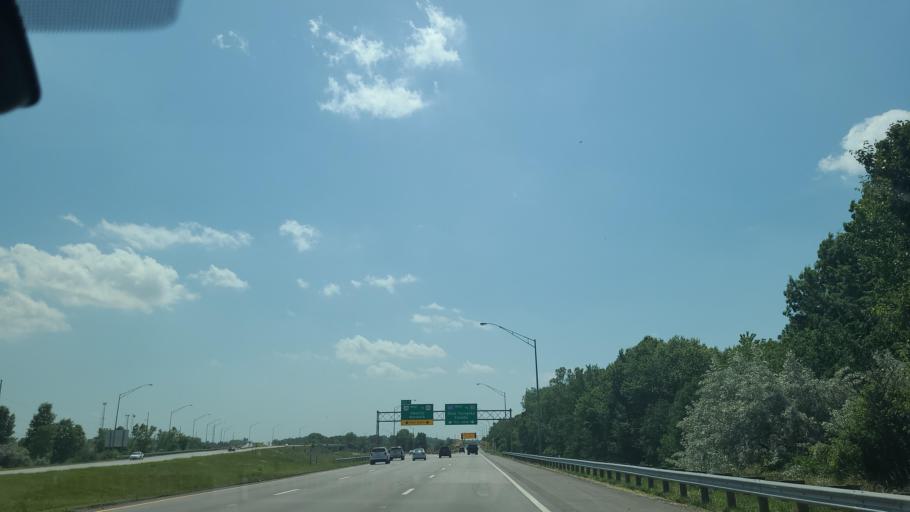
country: US
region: Ohio
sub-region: Lorain County
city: North Ridgeville
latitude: 41.3863
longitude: -81.9810
